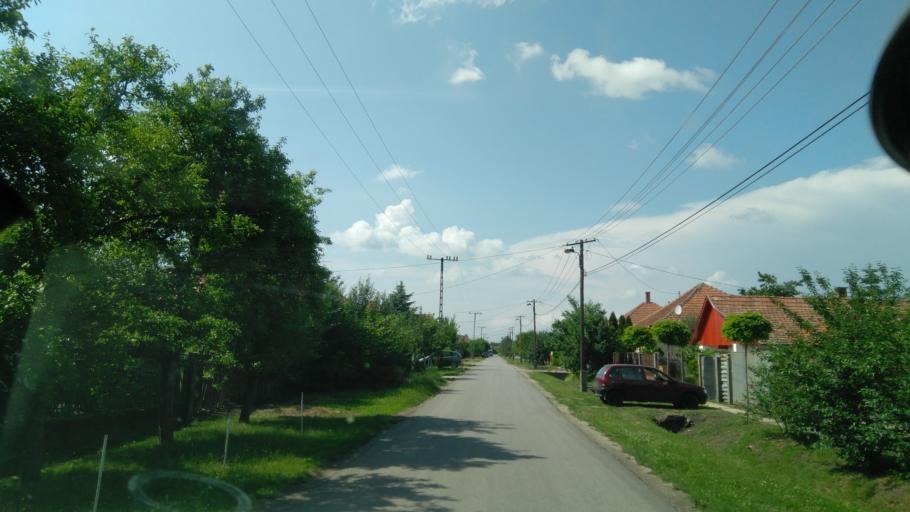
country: HU
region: Bekes
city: Doboz
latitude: 46.7326
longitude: 21.2327
